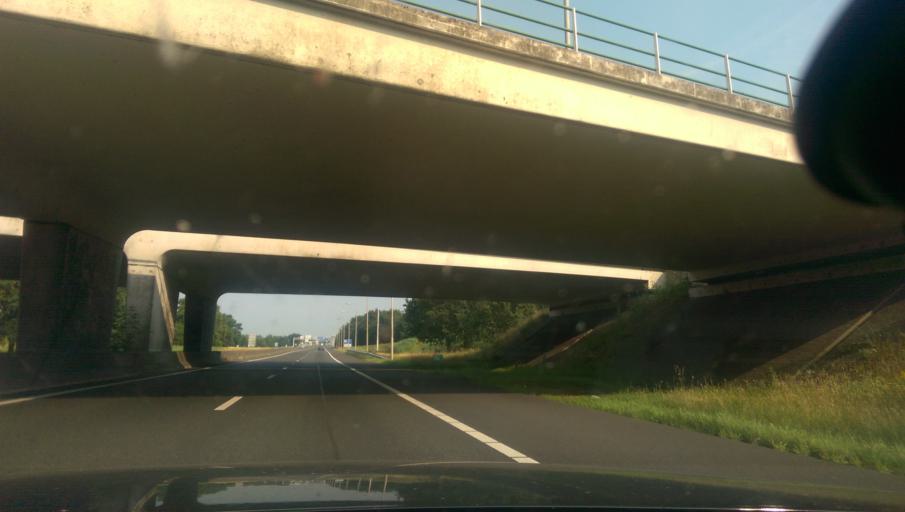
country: NL
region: Limburg
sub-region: Gemeente Venlo
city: Venlo
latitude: 51.3896
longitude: 6.1985
